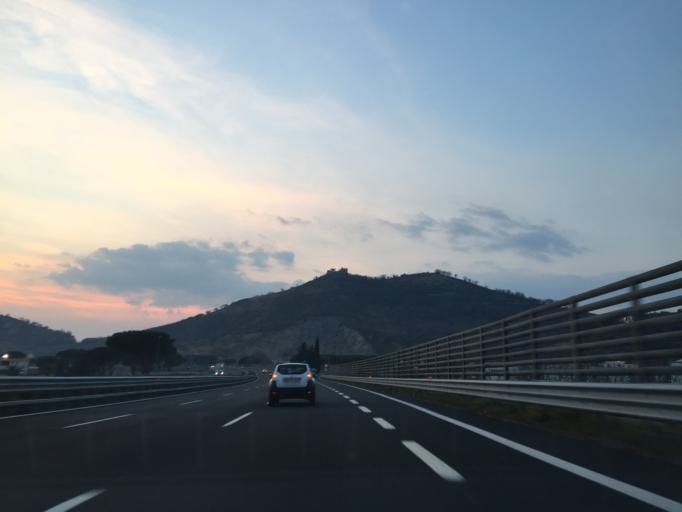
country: IT
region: Campania
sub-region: Provincia di Salerno
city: Lanzara
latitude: 40.7701
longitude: 14.6711
